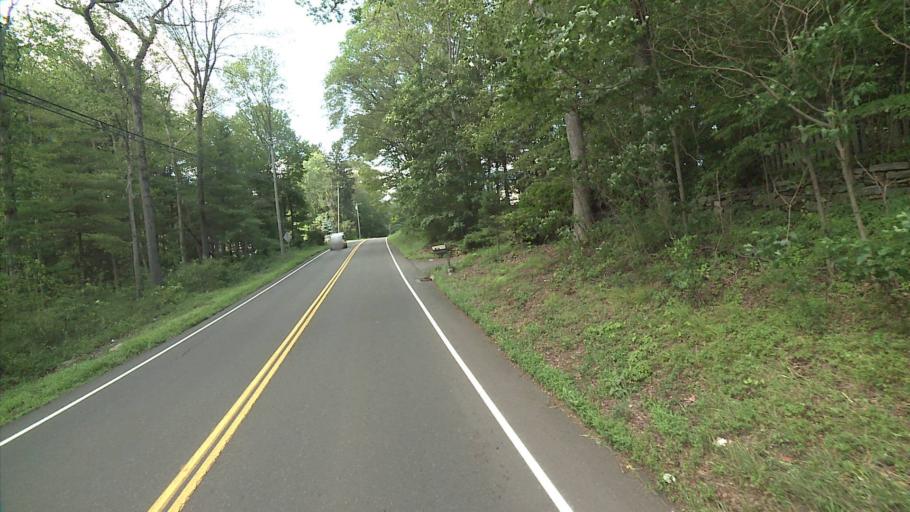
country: US
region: Connecticut
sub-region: Middlesex County
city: Higganum
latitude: 41.4144
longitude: -72.5635
